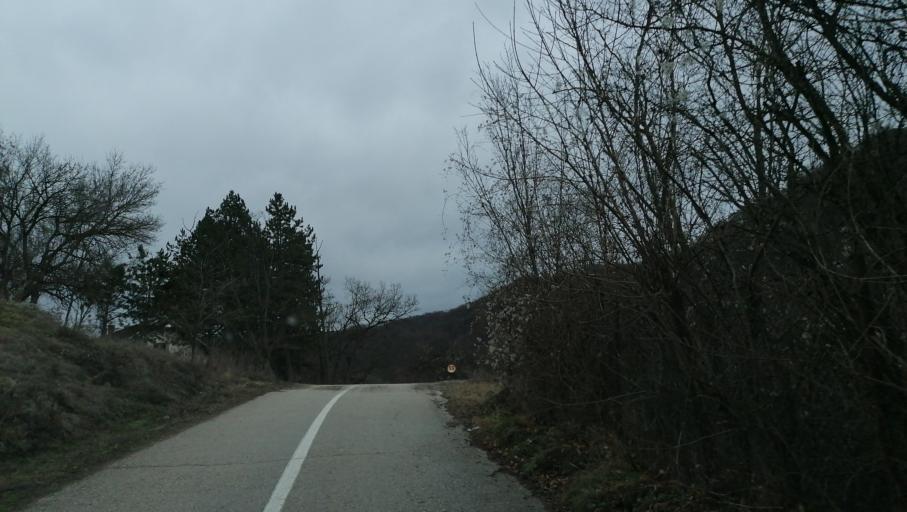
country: RS
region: Central Serbia
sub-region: Pirotski Okrug
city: Dimitrovgrad
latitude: 42.9513
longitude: 22.7753
